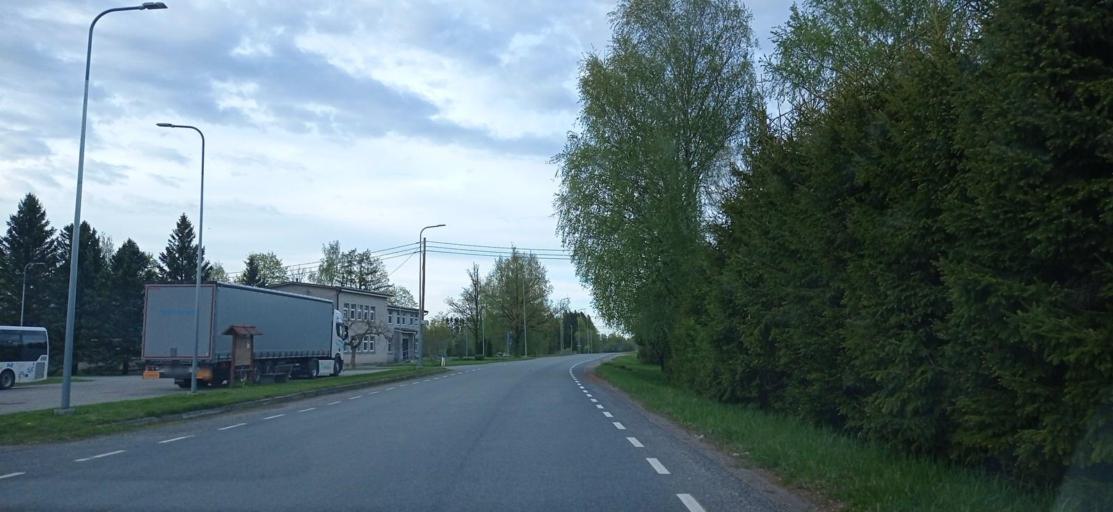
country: EE
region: Paernumaa
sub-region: Tootsi vald
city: Tootsi
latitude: 58.5268
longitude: 24.7024
